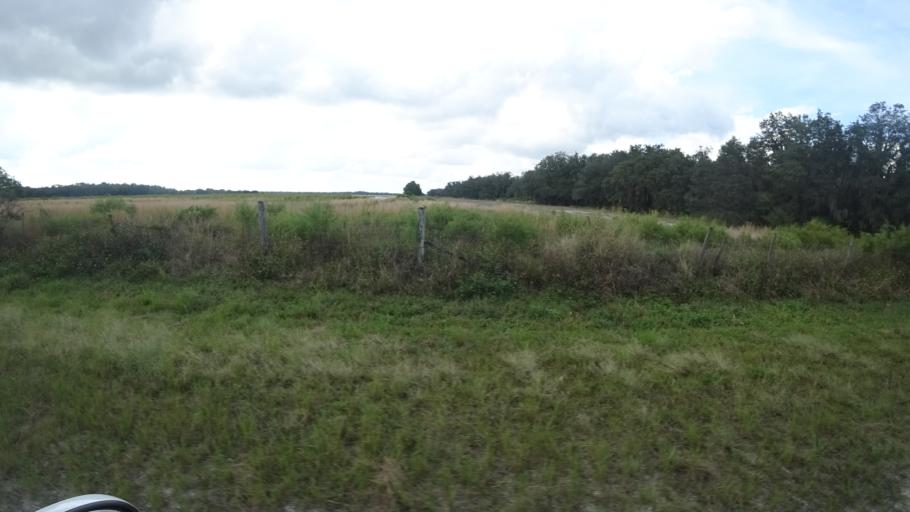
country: US
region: Florida
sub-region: Hillsborough County
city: Wimauma
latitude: 27.5722
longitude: -82.1741
